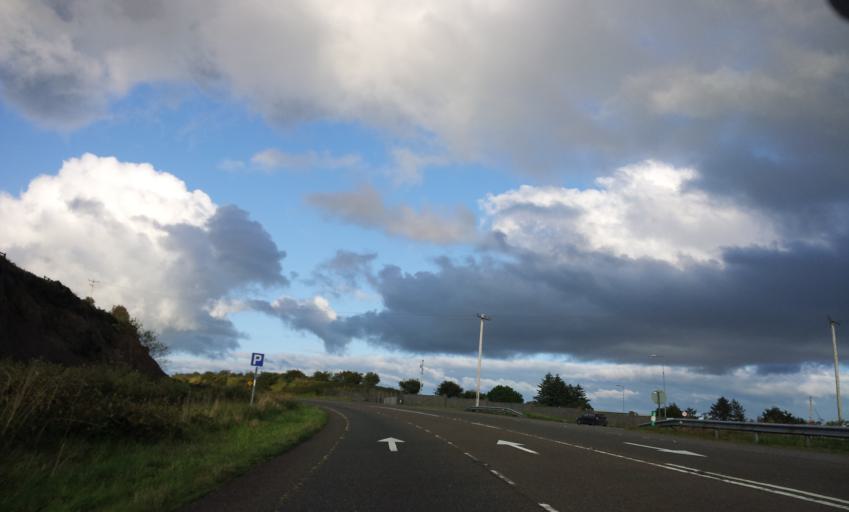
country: IE
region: Munster
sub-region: Ciarrai
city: Castleisland
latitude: 52.2647
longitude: -9.4301
